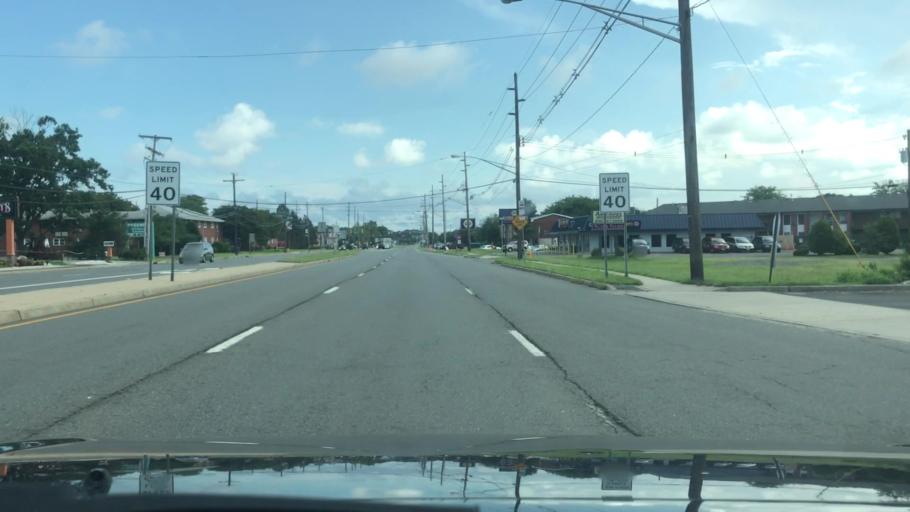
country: US
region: New Jersey
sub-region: Ocean County
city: Leisure Village East
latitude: 40.0483
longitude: -74.1423
